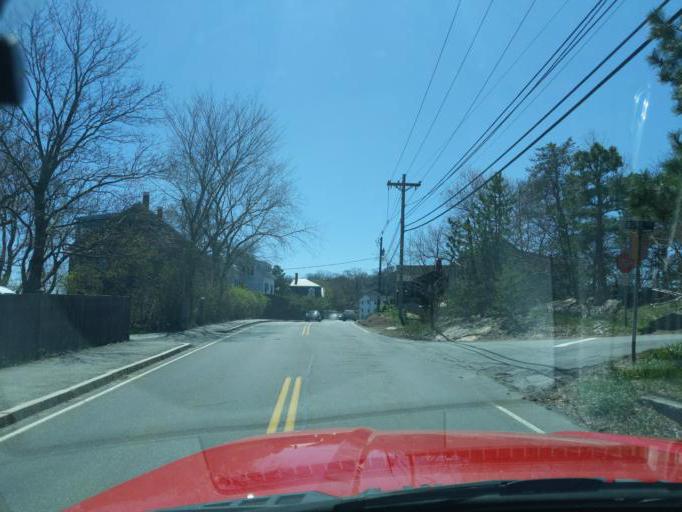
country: US
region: Massachusetts
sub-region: Essex County
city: Rockport
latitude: 42.6682
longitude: -70.6247
